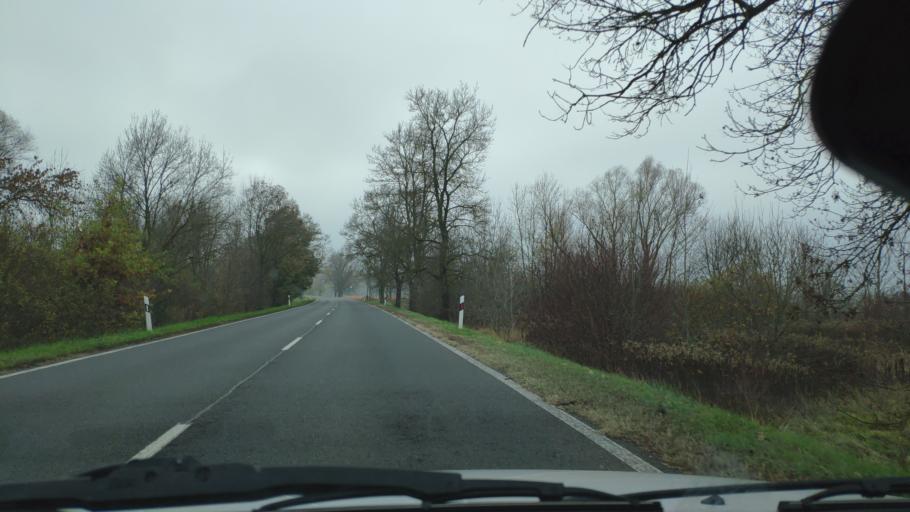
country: HU
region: Somogy
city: Balatonbereny
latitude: 46.6393
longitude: 17.2967
